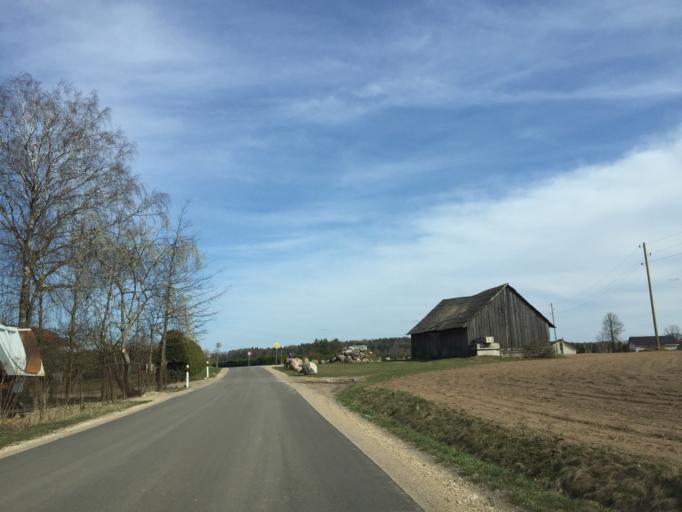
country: LV
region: Ikskile
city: Ikskile
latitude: 56.8406
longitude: 24.5169
